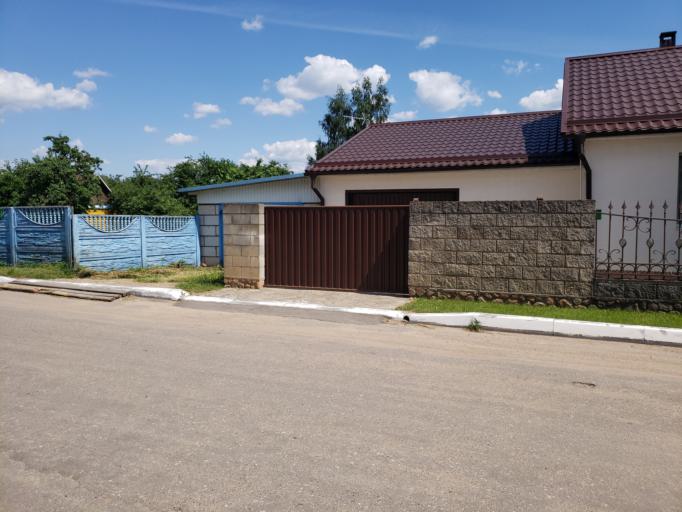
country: BY
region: Minsk
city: Chervyen'
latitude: 53.7164
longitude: 28.4023
